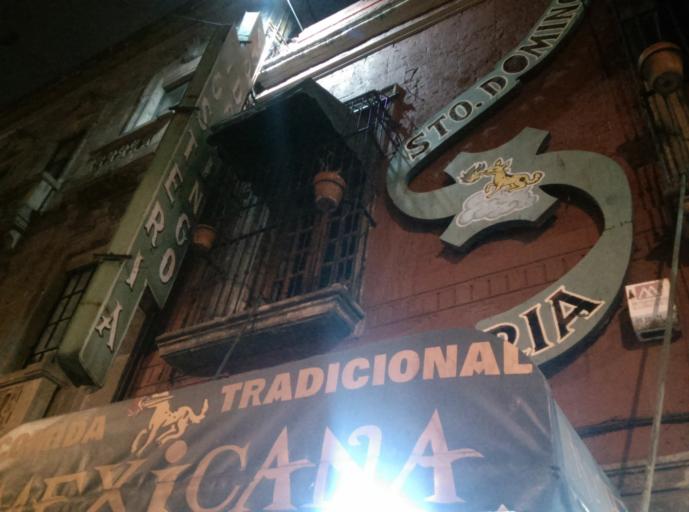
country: MX
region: Mexico City
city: Mexico City
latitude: 19.4378
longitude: -99.1350
